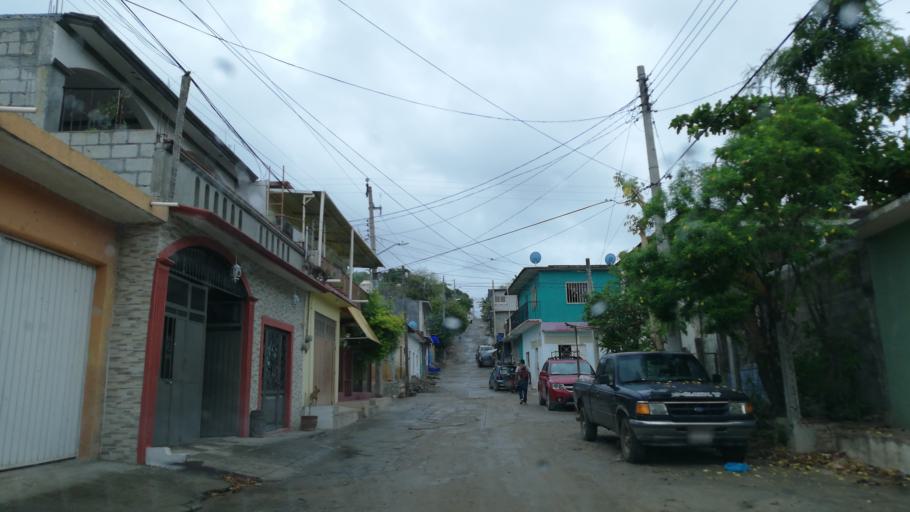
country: MX
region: Oaxaca
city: San Blas Atempa
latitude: 16.3362
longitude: -95.2242
